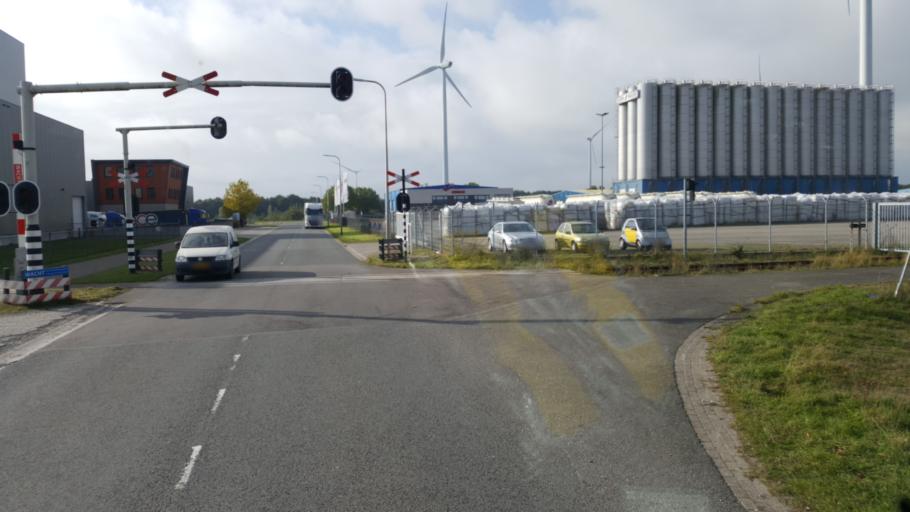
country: NL
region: Drenthe
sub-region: Gemeente Coevorden
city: Coevorden
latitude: 52.6450
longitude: 6.7345
